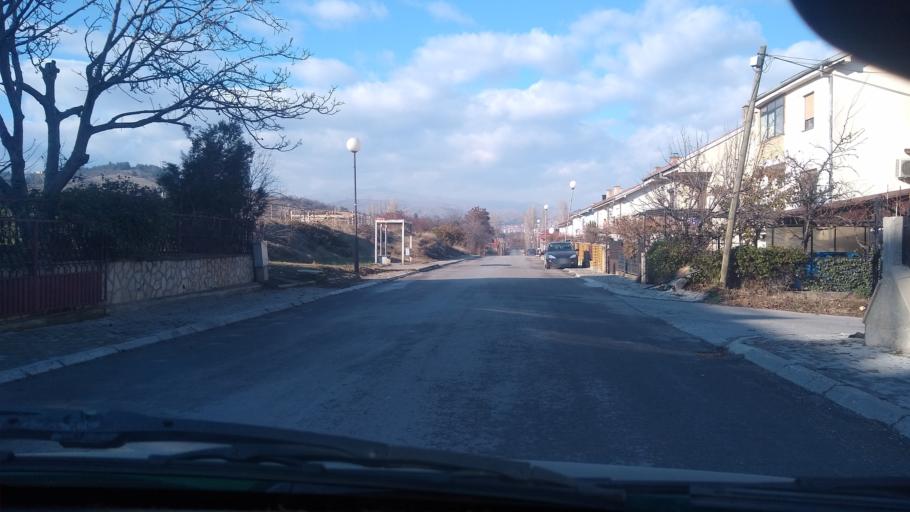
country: MK
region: Bitola
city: Bitola
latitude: 41.0066
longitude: 21.3485
